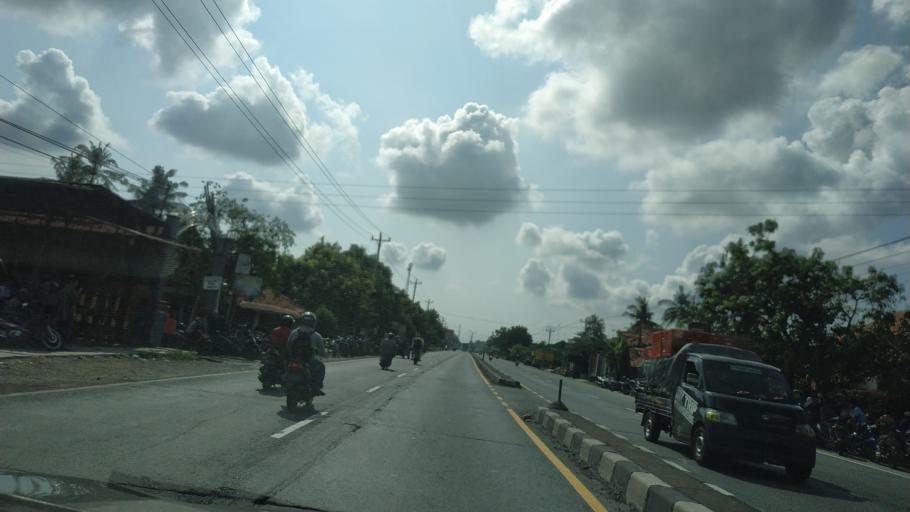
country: ID
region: Central Java
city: Comal
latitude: -6.8866
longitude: 109.5511
